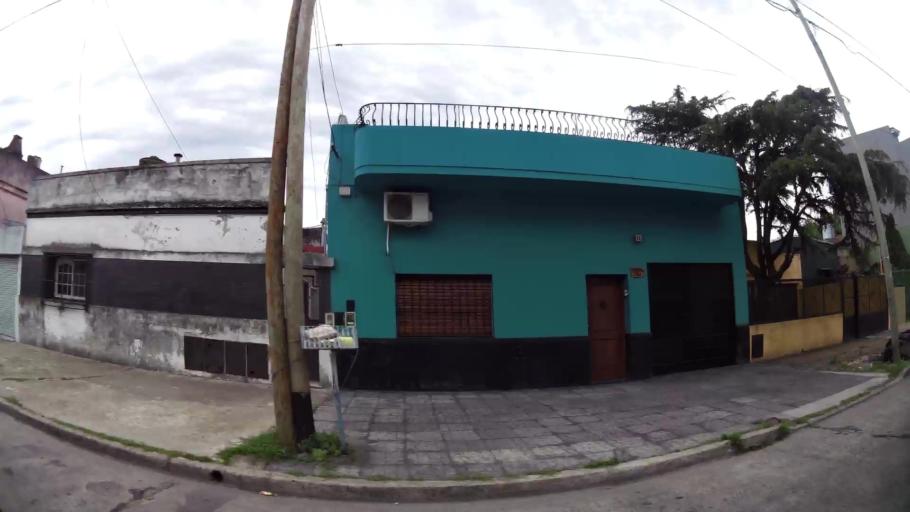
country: AR
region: Buenos Aires
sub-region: Partido de Lanus
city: Lanus
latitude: -34.6837
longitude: -58.3916
